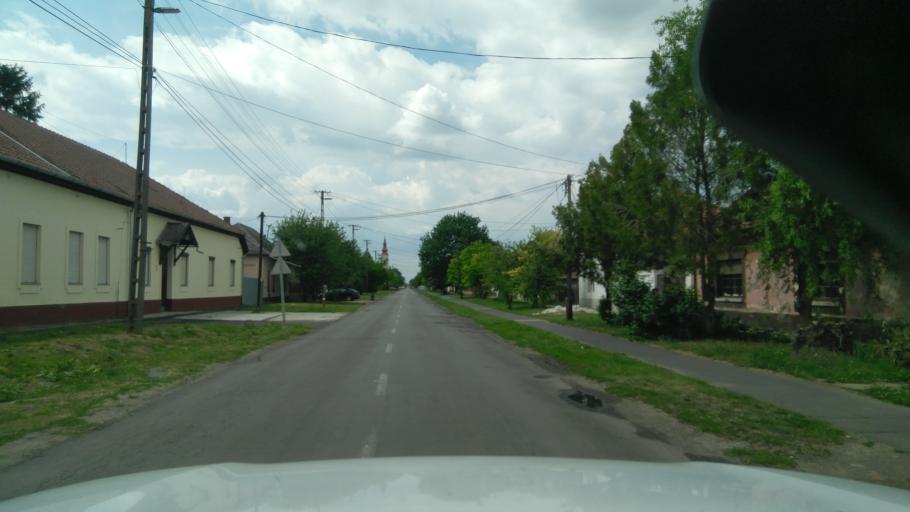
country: HU
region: Bekes
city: Magyarbanhegyes
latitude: 46.4532
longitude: 20.9702
